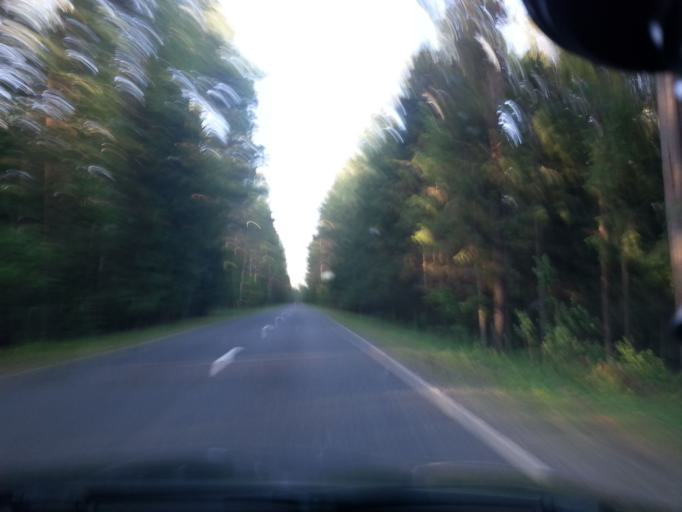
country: BY
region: Minsk
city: Narach
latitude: 54.9426
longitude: 26.5736
